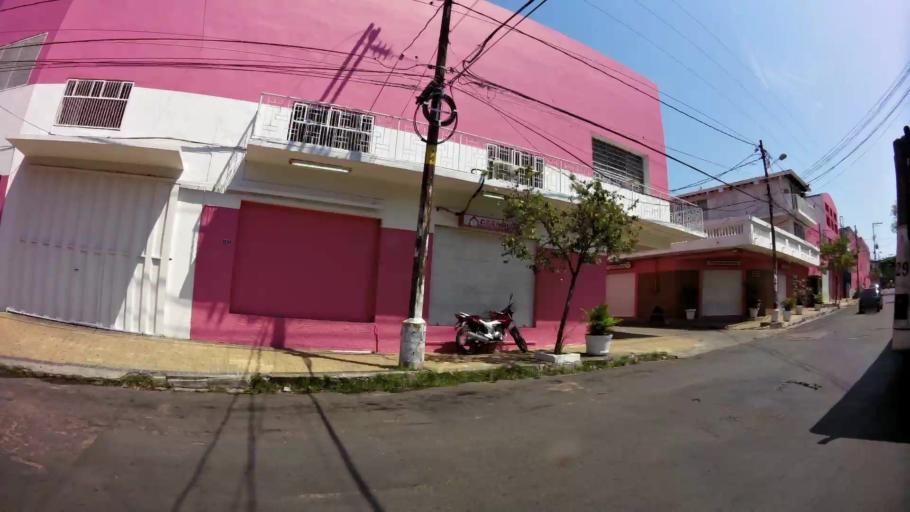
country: PY
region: Presidente Hayes
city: Nanawa
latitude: -25.2777
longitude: -57.6474
